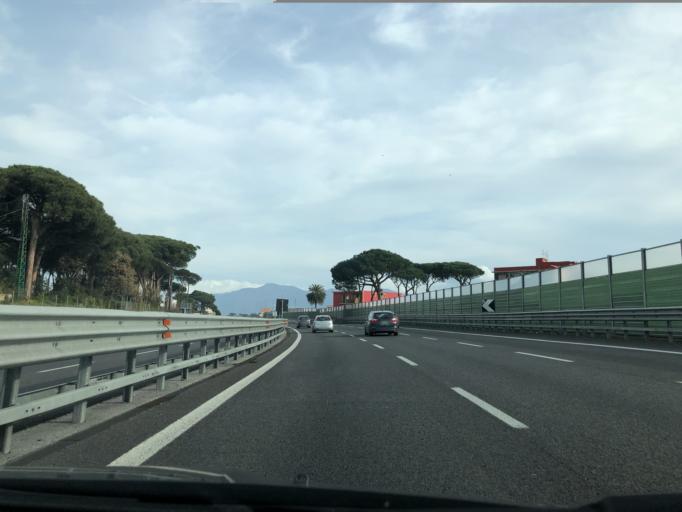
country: IT
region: Campania
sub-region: Provincia di Napoli
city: Torre del Greco
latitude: 40.7802
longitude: 14.3919
